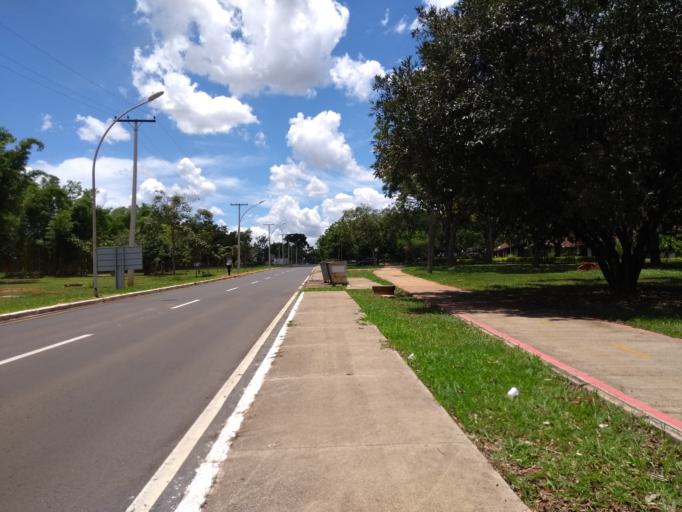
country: BR
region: Federal District
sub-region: Brasilia
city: Brasilia
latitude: -15.7693
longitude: -47.8691
